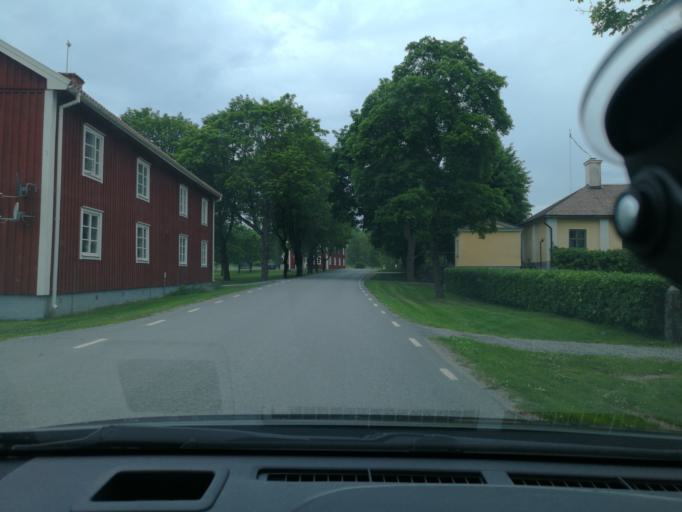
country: SE
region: Vaestmanland
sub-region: Vasteras
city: Skultuna
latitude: 59.7772
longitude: 16.3809
